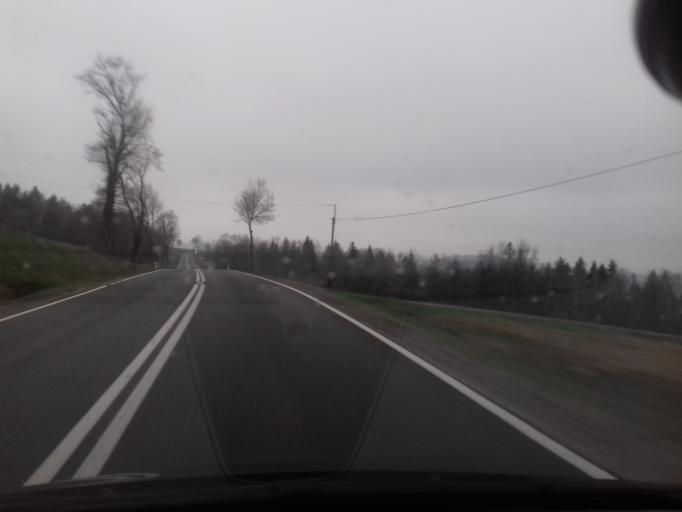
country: PL
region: Lesser Poland Voivodeship
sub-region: Powiat limanowski
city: Tymbark
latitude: 49.7233
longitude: 20.3133
